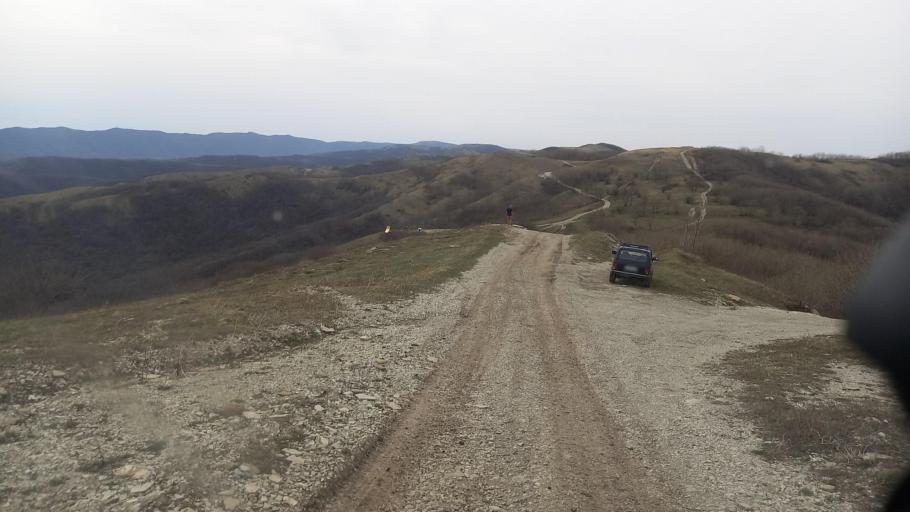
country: RU
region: Krasnodarskiy
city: Divnomorskoye
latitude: 44.6087
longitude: 38.2468
